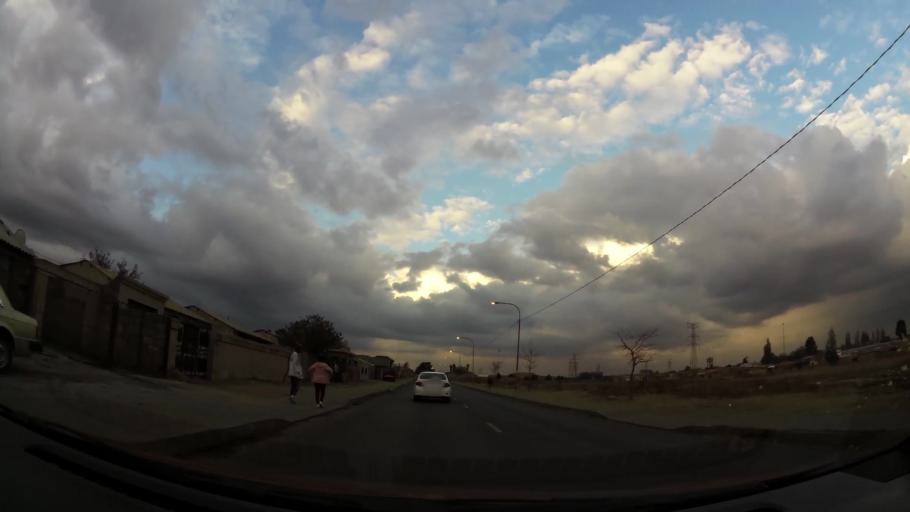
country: ZA
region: Gauteng
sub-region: City of Johannesburg Metropolitan Municipality
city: Soweto
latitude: -26.2404
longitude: 27.8496
